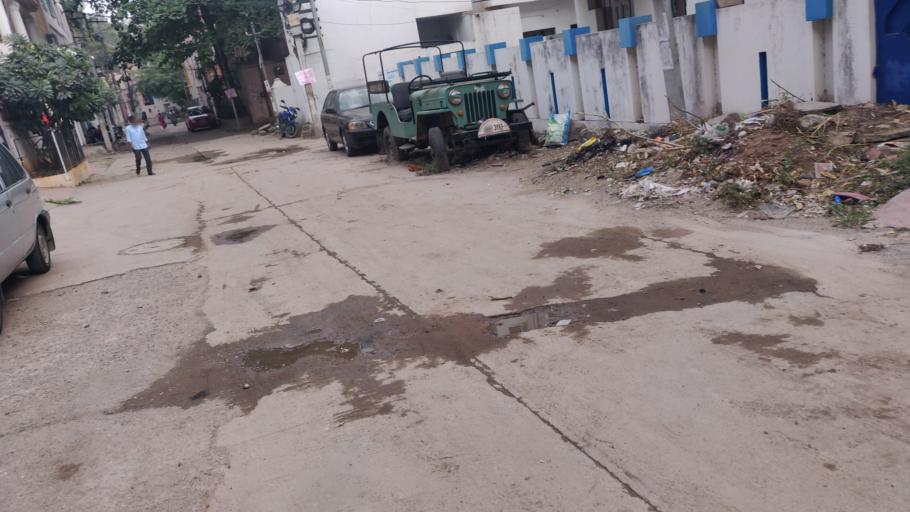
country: IN
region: Telangana
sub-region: Hyderabad
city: Hyderabad
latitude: 17.3909
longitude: 78.4351
